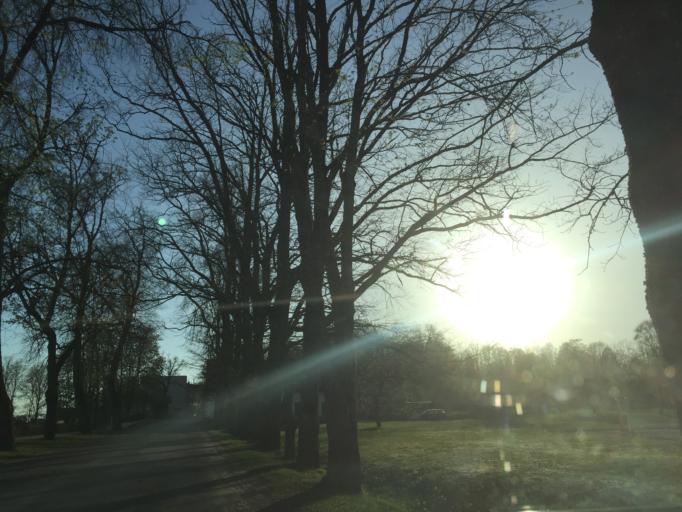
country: LV
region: Koknese
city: Koknese
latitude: 56.7231
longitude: 25.4879
